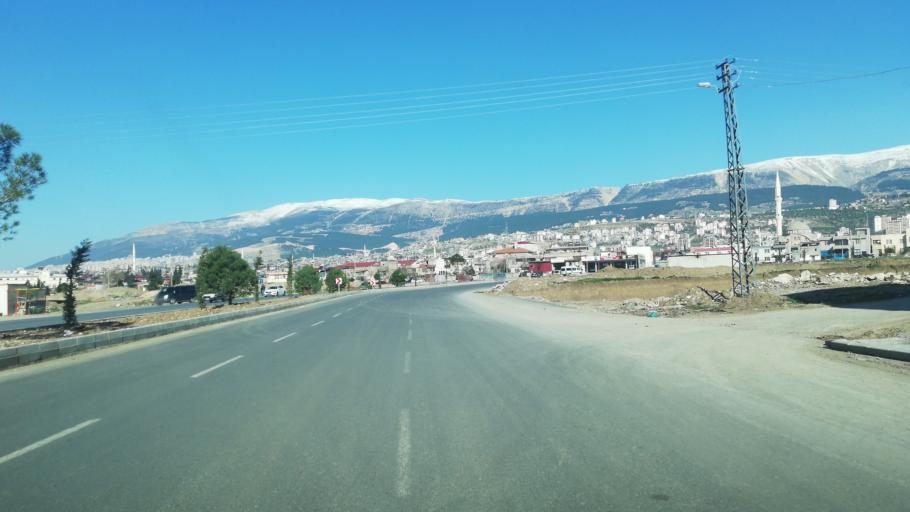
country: TR
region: Kahramanmaras
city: Kahramanmaras
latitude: 37.5685
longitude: 36.9641
